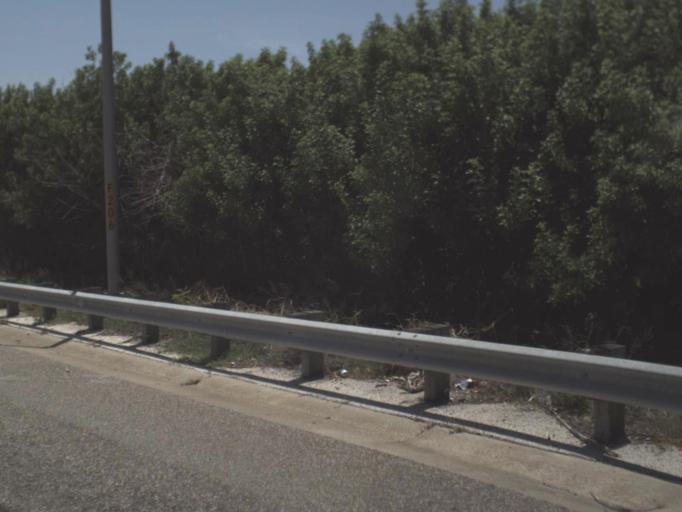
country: US
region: Florida
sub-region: Pinellas County
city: Tierra Verde
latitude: 27.6875
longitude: -82.6787
